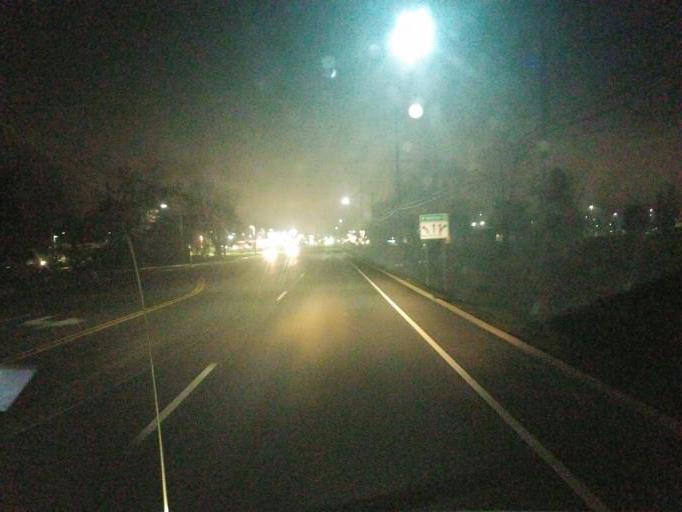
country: US
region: Ohio
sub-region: Williams County
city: Bryan
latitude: 41.4568
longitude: -84.5504
